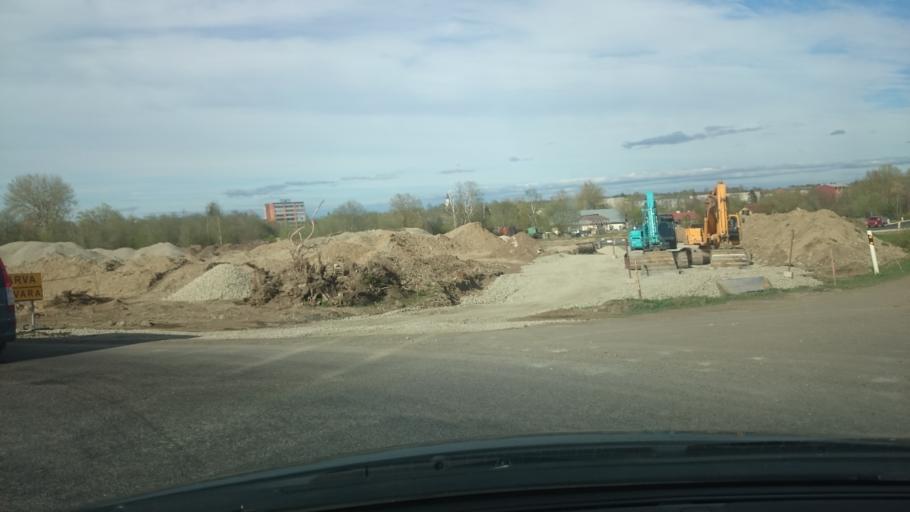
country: EE
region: Ida-Virumaa
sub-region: Sillamaee linn
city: Sillamae
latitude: 59.3913
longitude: 27.7499
